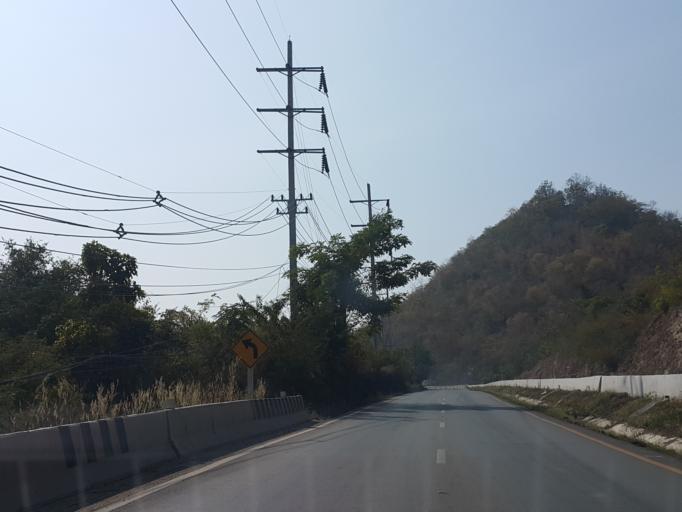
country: TH
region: Chiang Mai
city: Chom Thong
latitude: 18.3787
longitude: 98.6796
